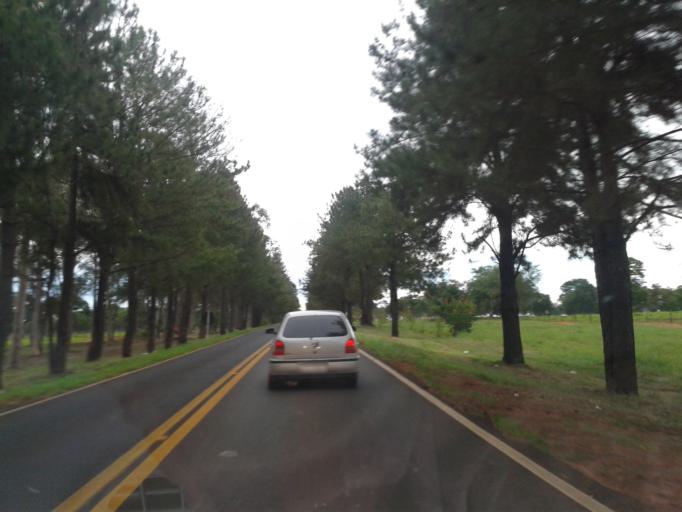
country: BR
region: Minas Gerais
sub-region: Santa Vitoria
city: Santa Vitoria
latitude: -18.8722
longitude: -50.1234
